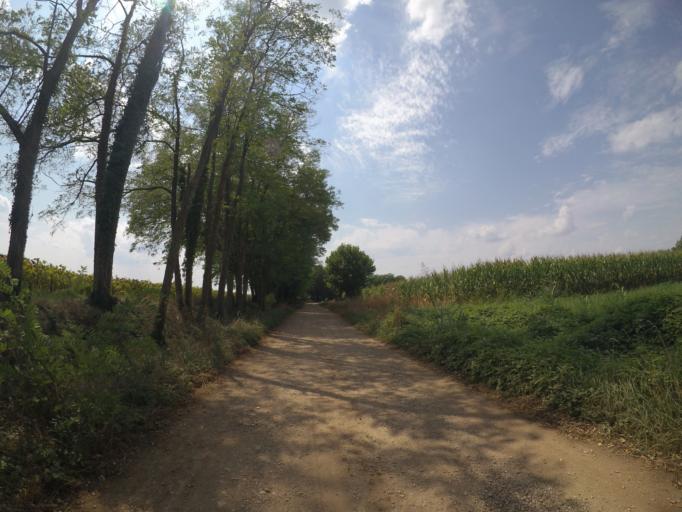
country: IT
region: Friuli Venezia Giulia
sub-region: Provincia di Udine
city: Bertiolo
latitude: 45.9575
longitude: 13.0766
